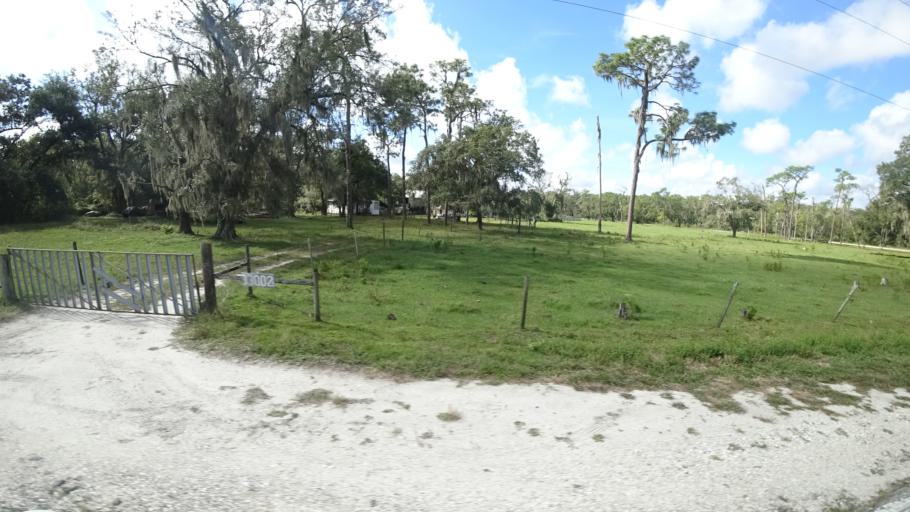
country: US
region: Florida
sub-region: Sarasota County
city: Lake Sarasota
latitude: 27.3398
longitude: -82.2036
